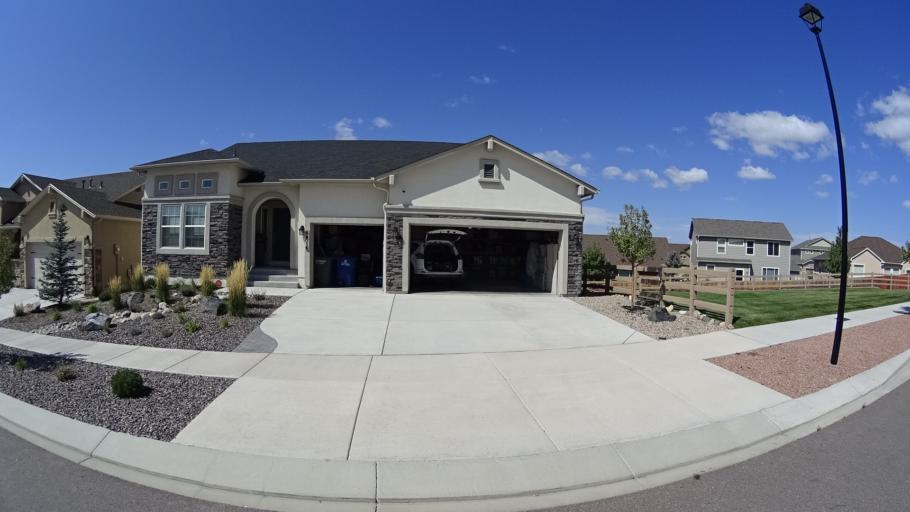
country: US
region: Colorado
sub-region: El Paso County
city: Cimarron Hills
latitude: 38.9304
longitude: -104.6846
